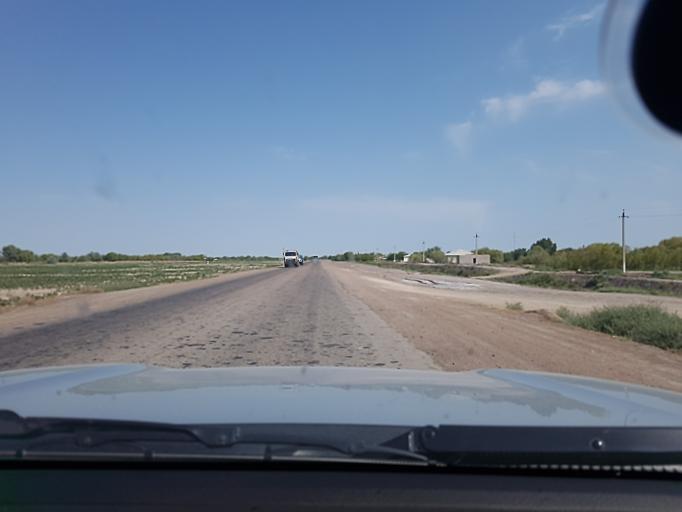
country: TM
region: Dasoguz
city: Boldumsaz
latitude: 42.1587
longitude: 59.6031
